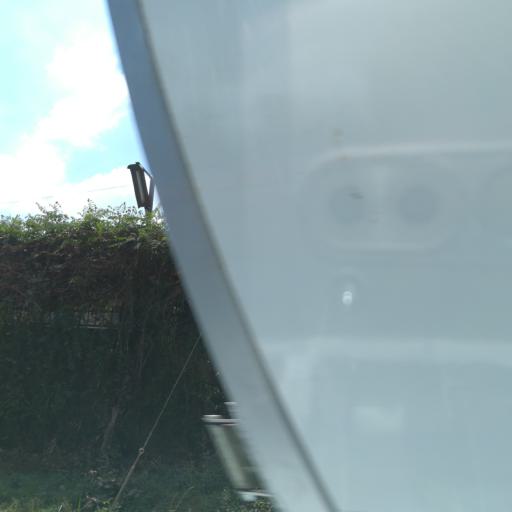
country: KE
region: Nairobi Area
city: Nairobi
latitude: -1.2970
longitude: 36.7956
